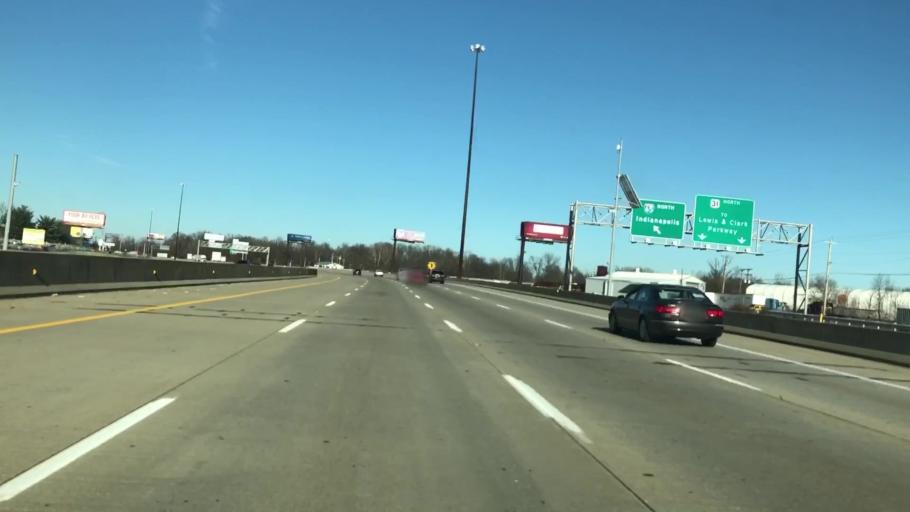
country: US
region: Indiana
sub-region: Clark County
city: Clarksville
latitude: 38.2966
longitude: -85.7566
